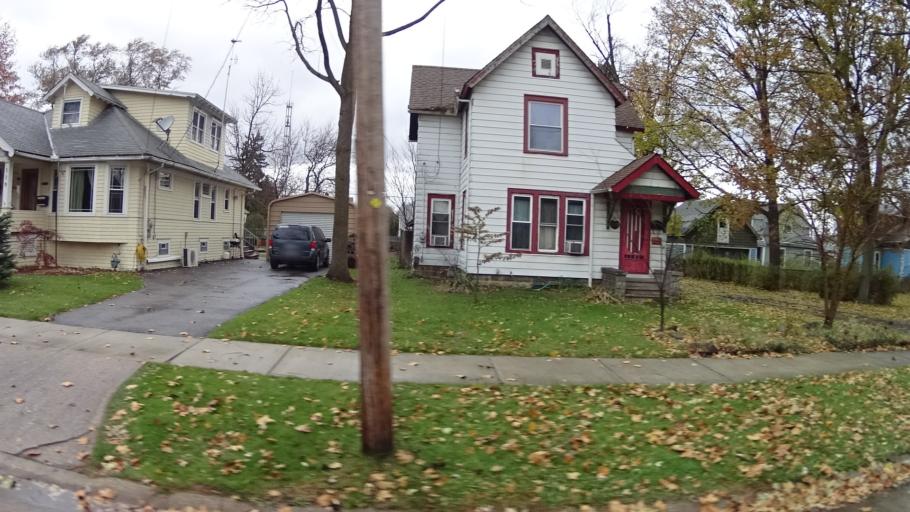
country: US
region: Ohio
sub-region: Lorain County
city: Elyria
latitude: 41.3838
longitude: -82.1287
